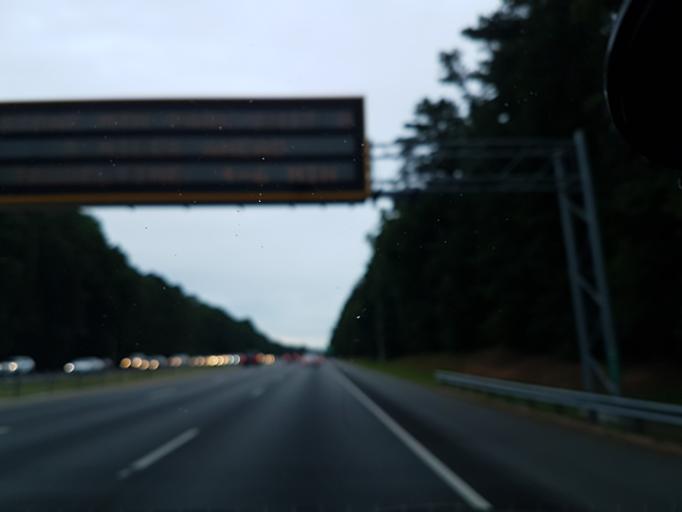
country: US
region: Georgia
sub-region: DeKalb County
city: Tucker
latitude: 33.8309
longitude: -84.2218
